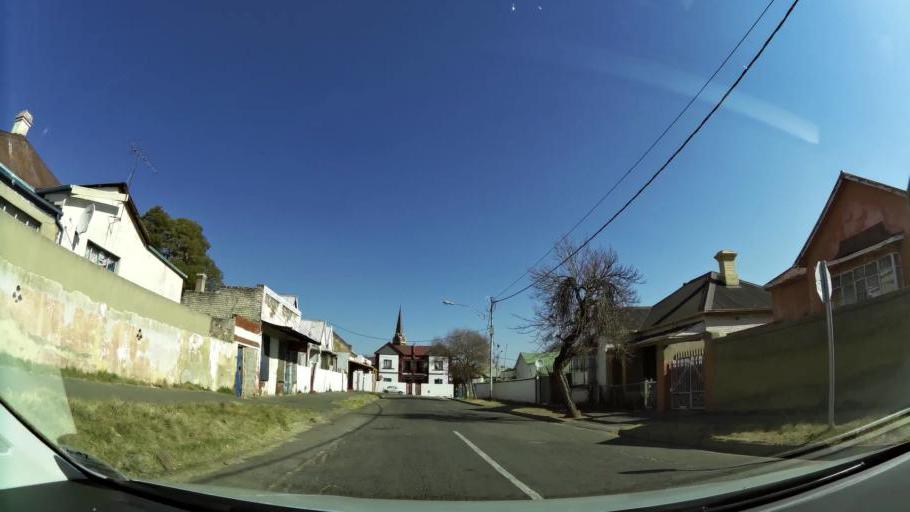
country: ZA
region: Gauteng
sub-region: City of Johannesburg Metropolitan Municipality
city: Johannesburg
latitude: -26.2008
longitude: 28.0706
